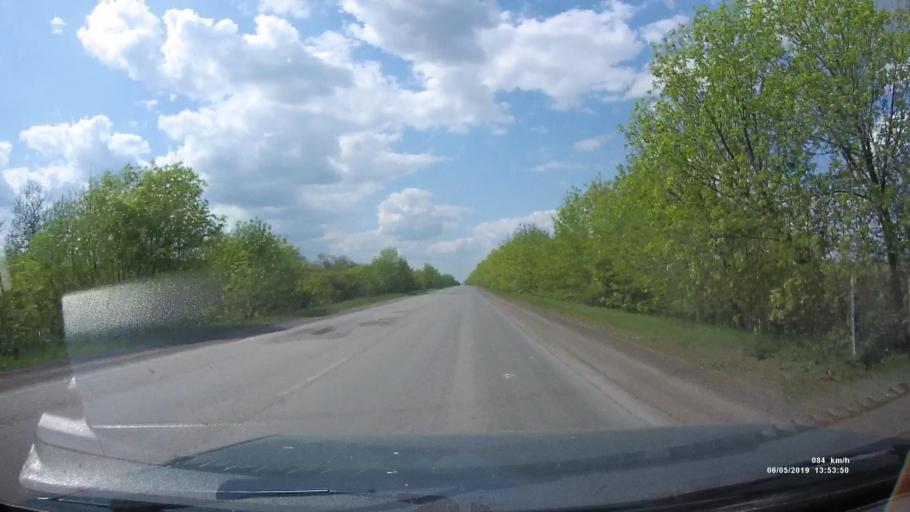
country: RU
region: Rostov
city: Melikhovskaya
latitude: 47.6708
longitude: 40.4562
